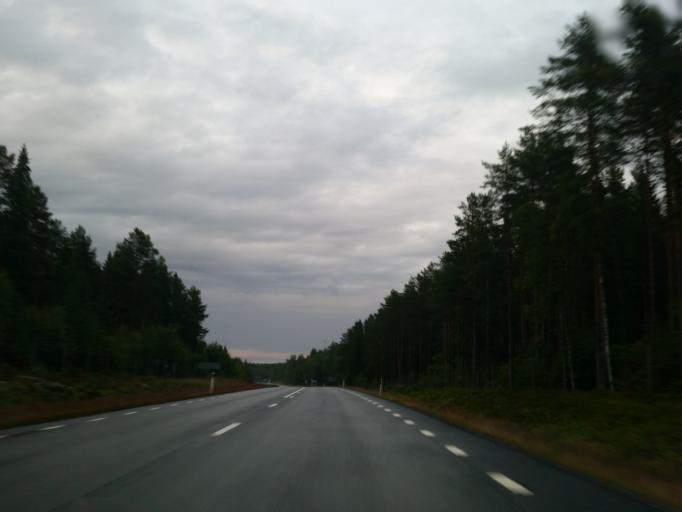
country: SE
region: Vaesterbotten
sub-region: Robertsfors Kommun
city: Robertsfors
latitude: 63.9983
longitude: 20.7861
